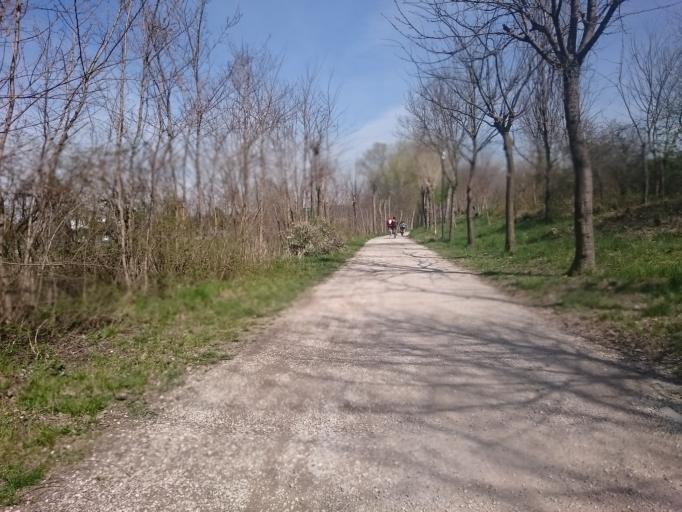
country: IT
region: Veneto
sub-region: Provincia di Padova
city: Limena
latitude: 45.4596
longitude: 11.8342
